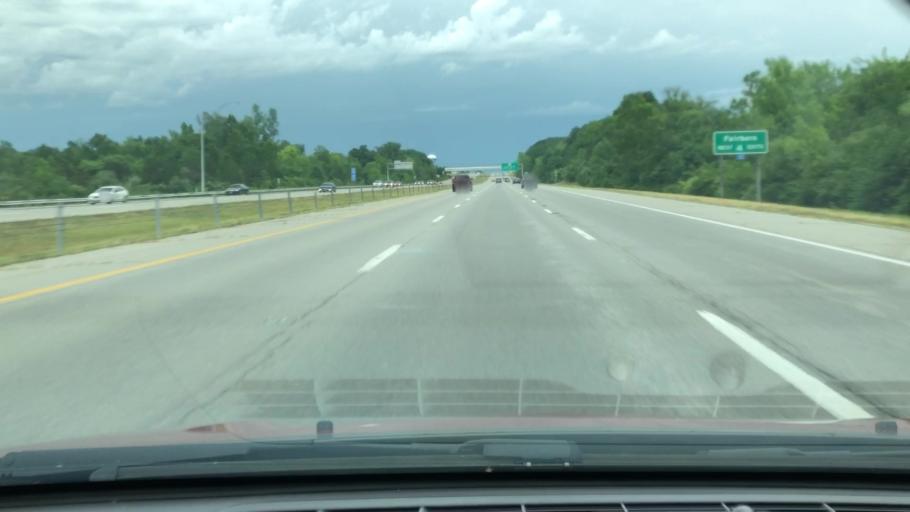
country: US
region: Ohio
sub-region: Montgomery County
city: Riverside
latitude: 39.7701
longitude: -84.0863
